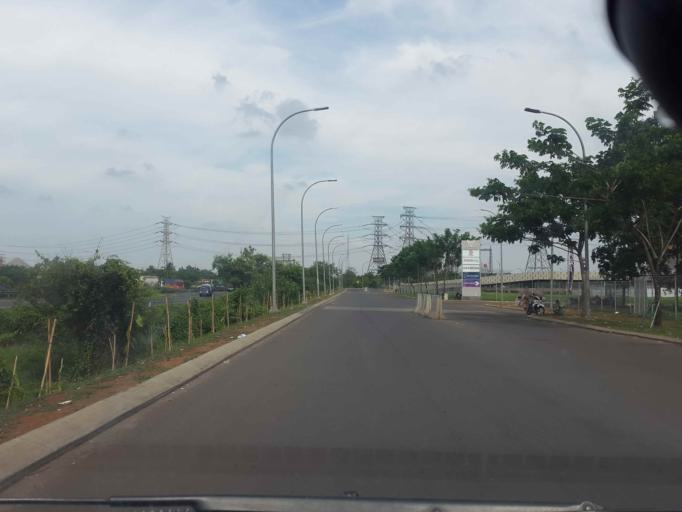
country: ID
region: West Java
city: Ciputat
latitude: -6.2203
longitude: 106.6528
